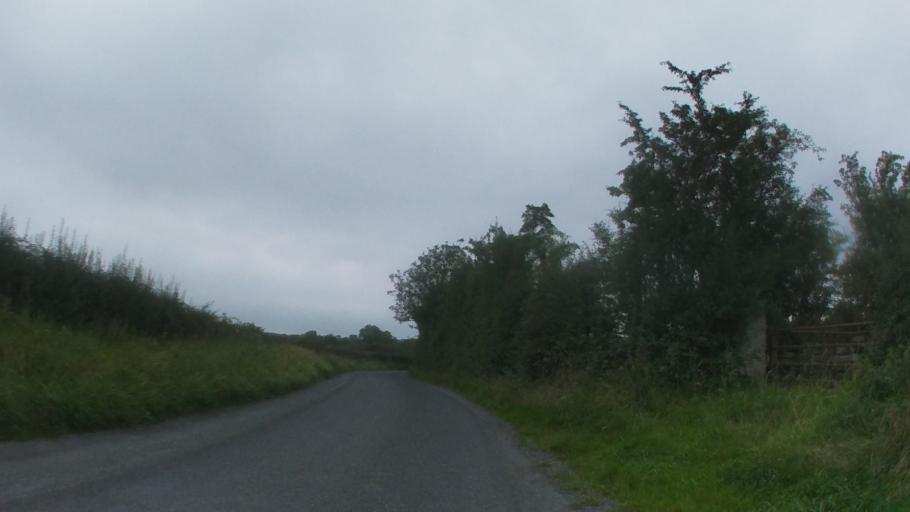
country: IE
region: Leinster
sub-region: Kilkenny
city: Kilkenny
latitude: 52.6986
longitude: -7.1971
